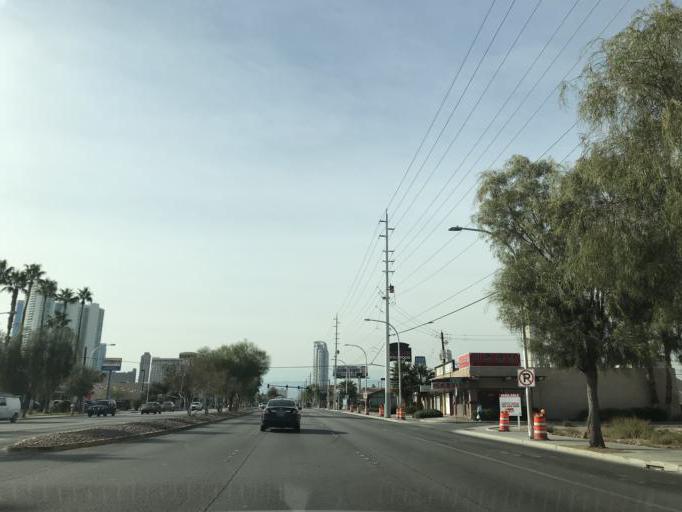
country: US
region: Nevada
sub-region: Clark County
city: Winchester
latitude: 36.1440
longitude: -115.1440
